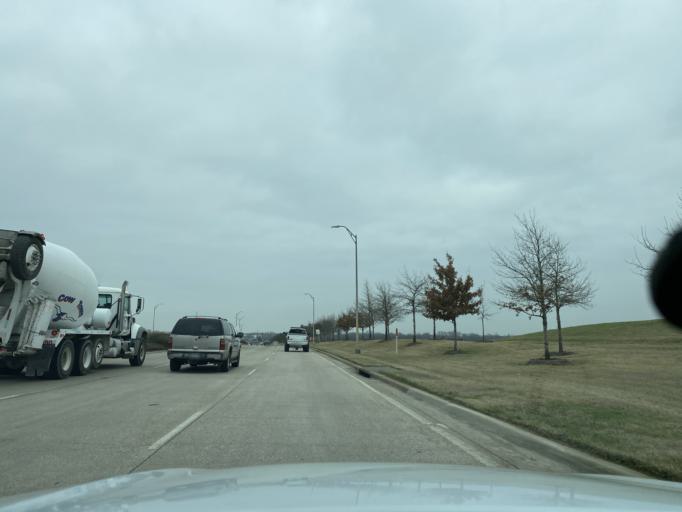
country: US
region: Texas
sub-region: Tarrant County
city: Euless
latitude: 32.7991
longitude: -97.0976
